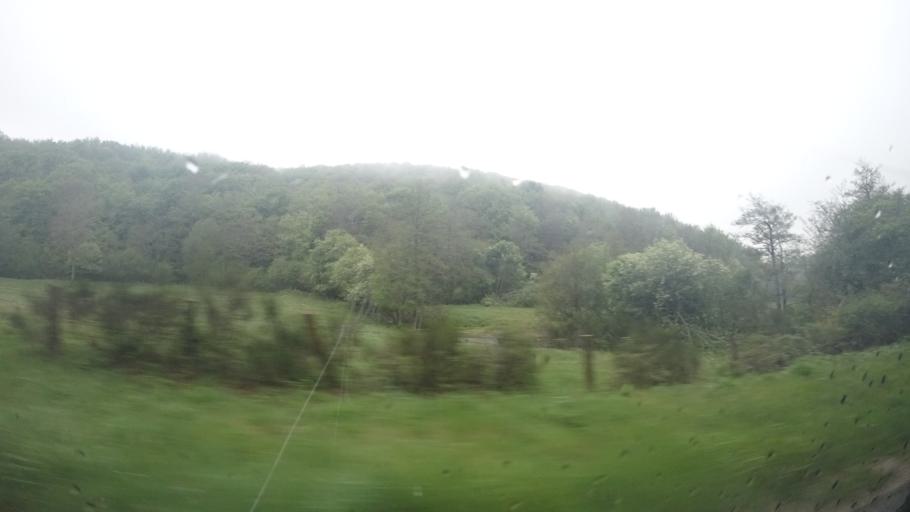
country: FR
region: Midi-Pyrenees
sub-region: Departement de l'Aveyron
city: Severac-le-Chateau
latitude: 44.2577
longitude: 2.9222
